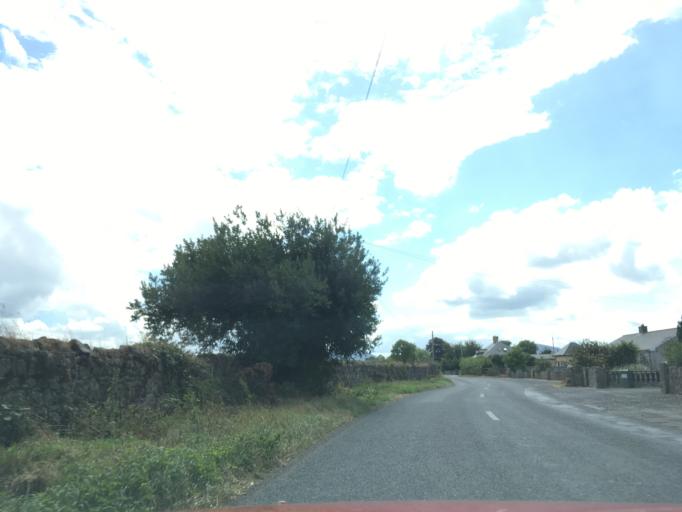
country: IE
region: Munster
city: Cahir
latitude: 52.3605
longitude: -7.9337
